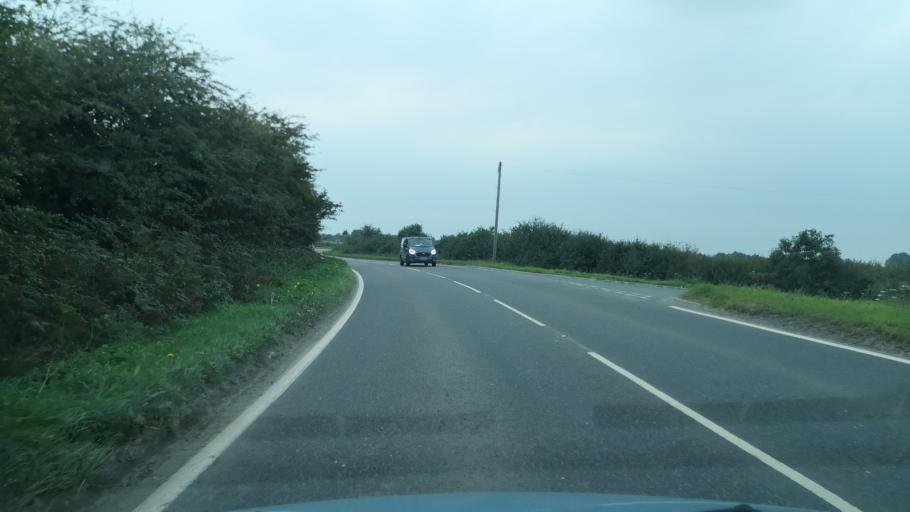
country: GB
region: England
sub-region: East Riding of Yorkshire
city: Pollington
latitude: 53.6938
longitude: -1.1056
